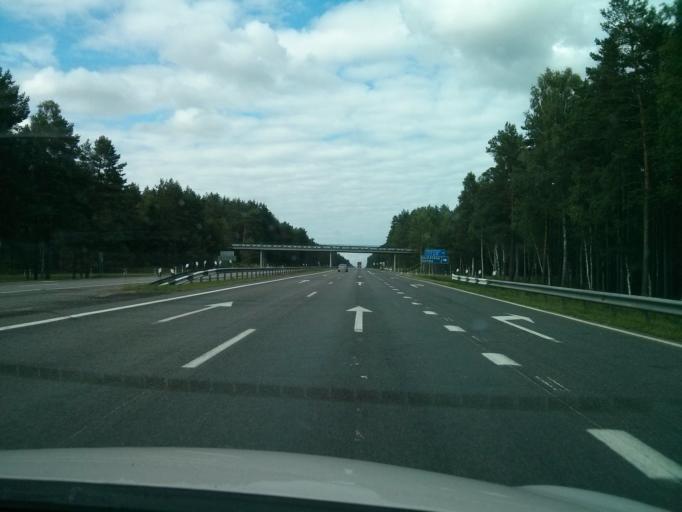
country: BY
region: Minsk
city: Zamostochcha
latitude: 53.8907
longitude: 27.9413
